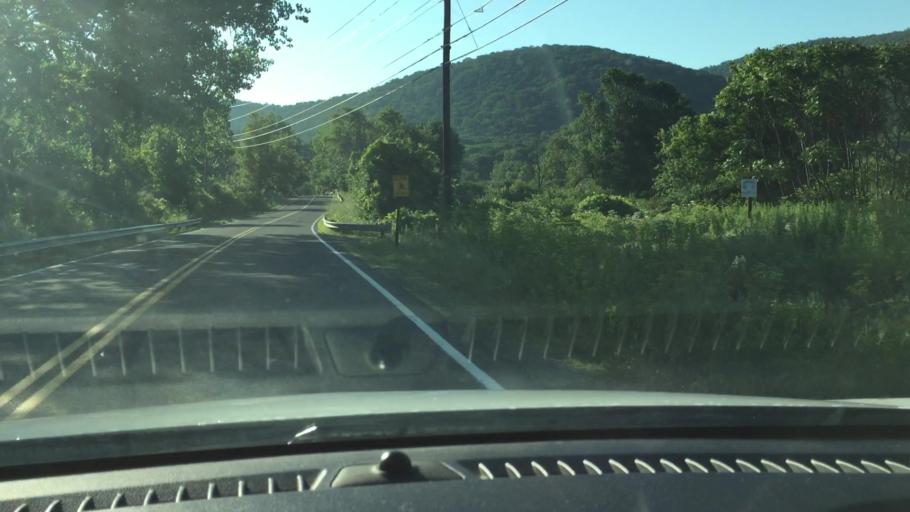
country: US
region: Massachusetts
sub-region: Berkshire County
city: Pittsfield
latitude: 42.3945
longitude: -73.2428
